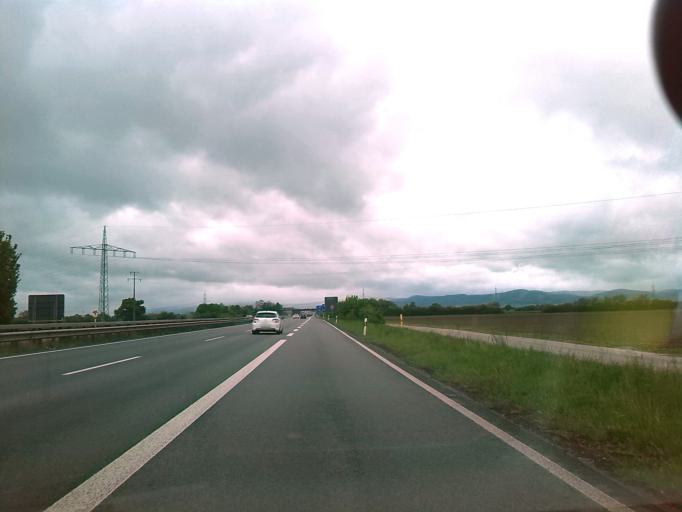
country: DE
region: Rheinland-Pfalz
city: Mutterstadt
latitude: 49.4500
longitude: 8.3421
